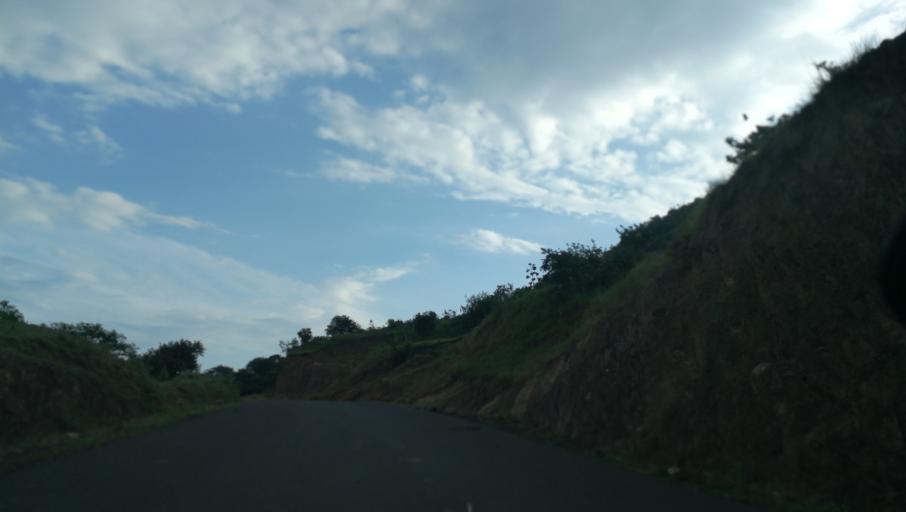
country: ET
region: Southern Nations, Nationalities, and People's Region
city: Areka
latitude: 6.8516
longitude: 37.2711
